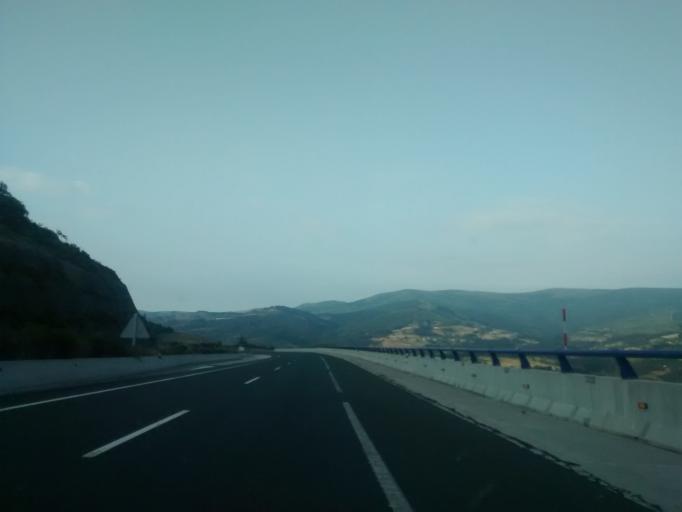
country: ES
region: Cantabria
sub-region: Provincia de Cantabria
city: Barcena de Pie de Concha
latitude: 43.1308
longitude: -4.0707
